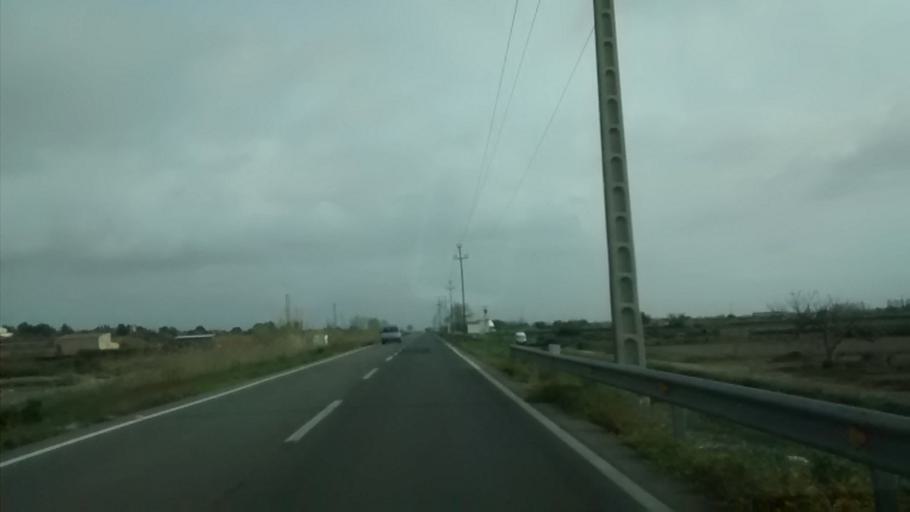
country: ES
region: Catalonia
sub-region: Provincia de Tarragona
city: Sant Carles de la Rapita
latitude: 40.6239
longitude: 0.5995
